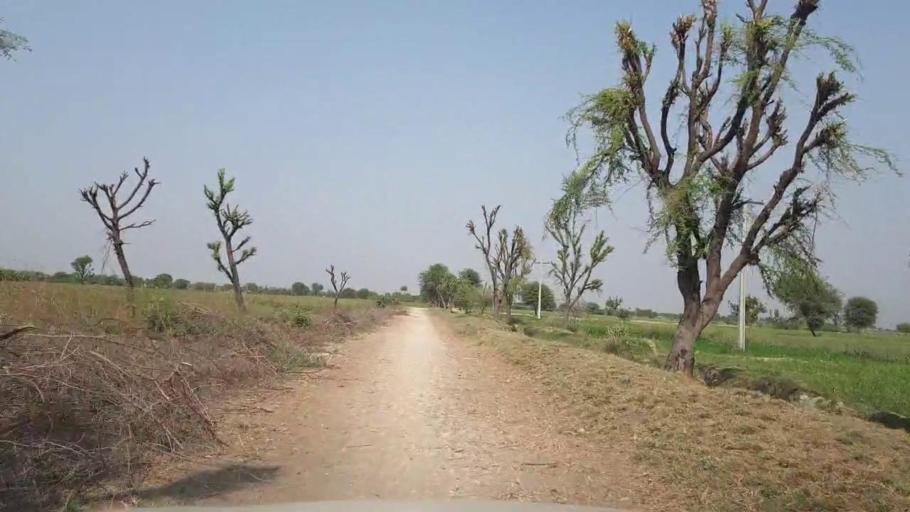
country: PK
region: Sindh
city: Dhoro Naro
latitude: 25.4833
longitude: 69.6074
